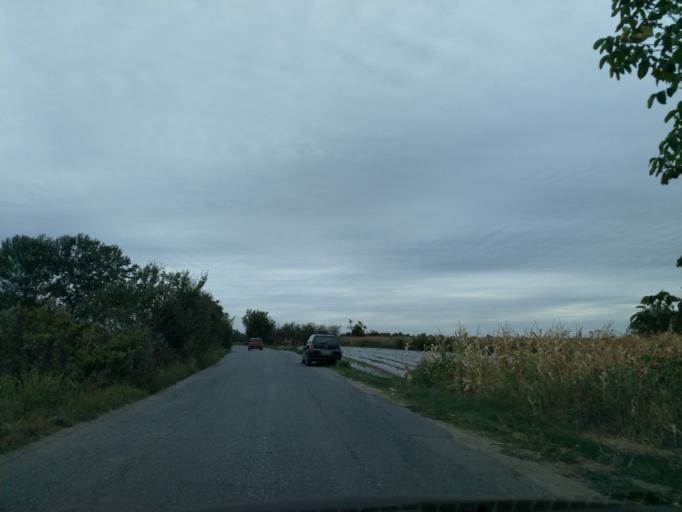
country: RS
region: Central Serbia
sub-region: Pomoravski Okrug
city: Paracin
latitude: 43.8329
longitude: 21.3300
